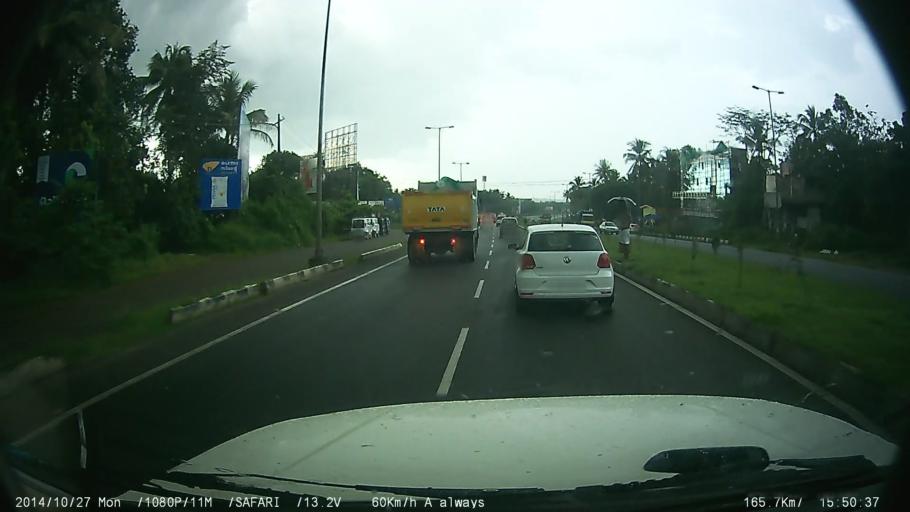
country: IN
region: Kerala
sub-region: Ernakulam
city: Angamali
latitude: 10.2445
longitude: 76.3719
